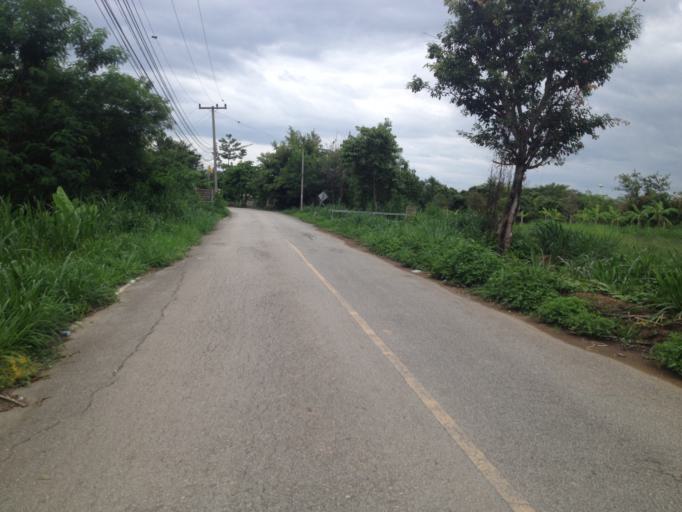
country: TH
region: Chiang Mai
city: Hang Dong
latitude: 18.7136
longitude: 98.9109
